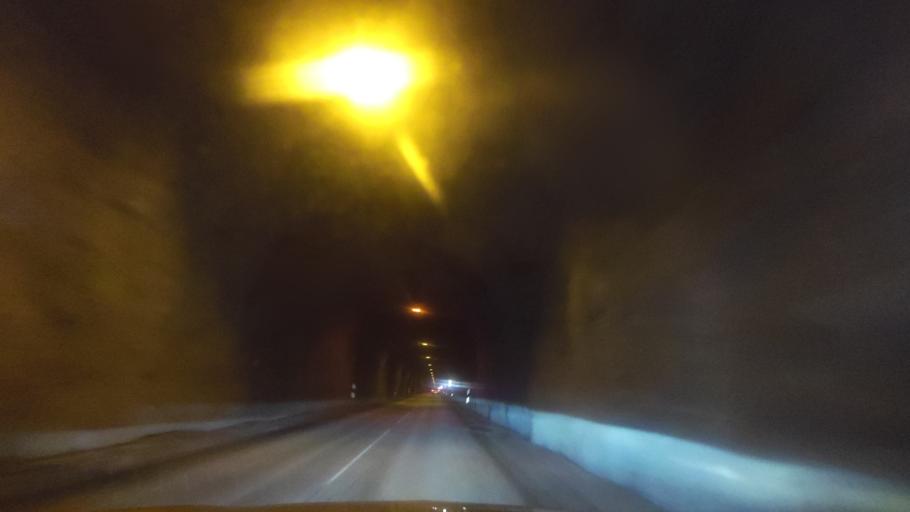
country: IS
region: Westfjords
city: Isafjoerdur
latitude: 66.0570
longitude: -23.2355
